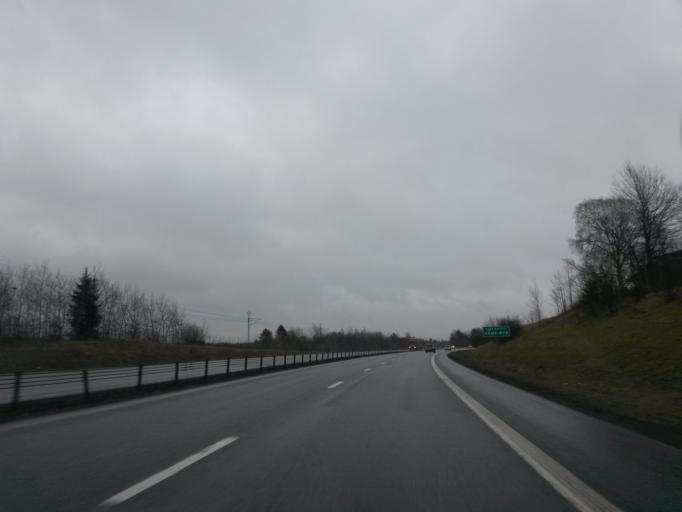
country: SE
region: Vaestra Goetaland
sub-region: Trollhattan
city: Sjuntorp
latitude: 58.3349
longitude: 12.1160
